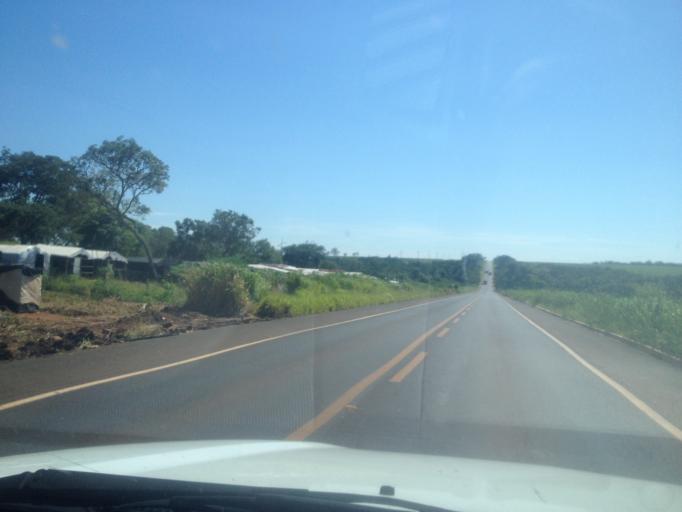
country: BR
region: Minas Gerais
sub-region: Santa Vitoria
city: Santa Vitoria
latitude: -18.9008
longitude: -50.1915
